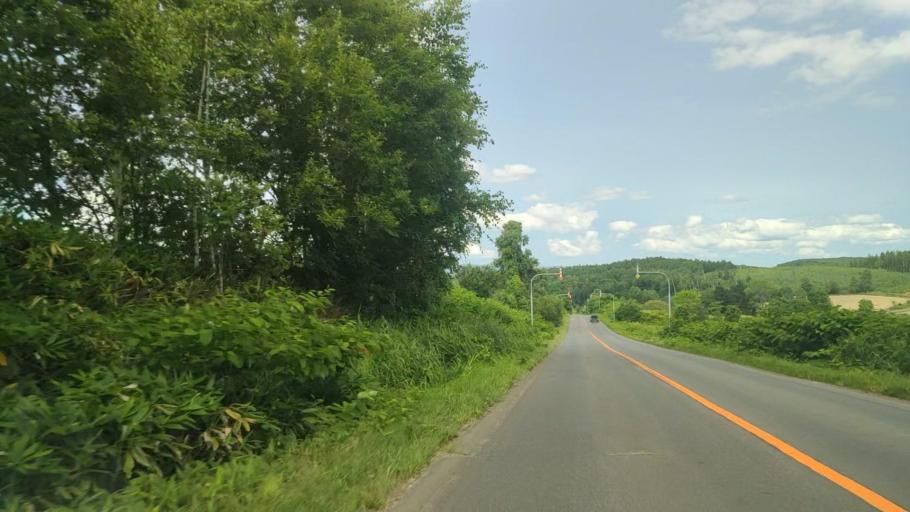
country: JP
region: Hokkaido
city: Nayoro
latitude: 44.2511
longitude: 142.4184
